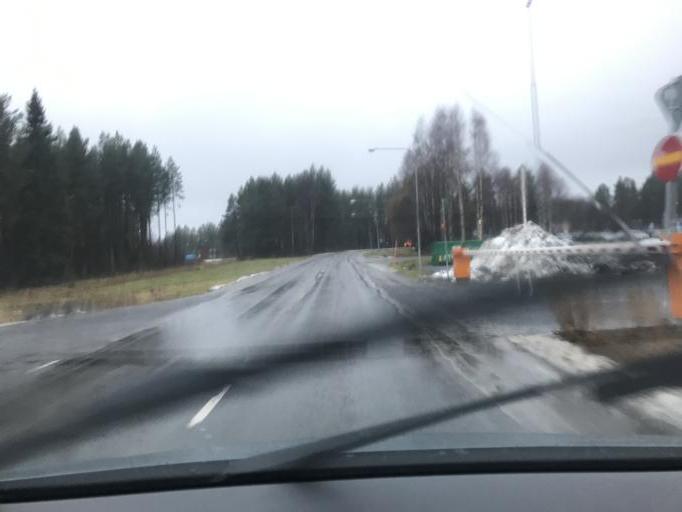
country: SE
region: Norrbotten
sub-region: Lulea Kommun
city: Bergnaset
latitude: 65.6167
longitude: 22.1224
